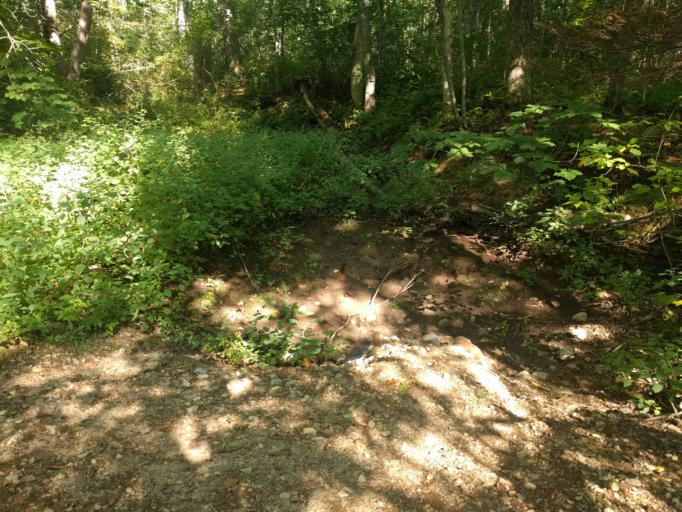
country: US
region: Maine
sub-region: Waldo County
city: Belfast
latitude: 44.4316
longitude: -68.9465
